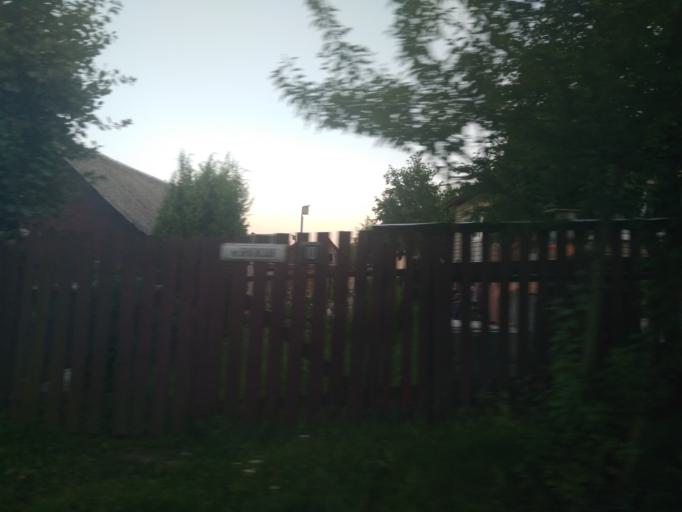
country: BY
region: Minsk
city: Minsk
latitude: 53.9391
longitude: 27.5524
